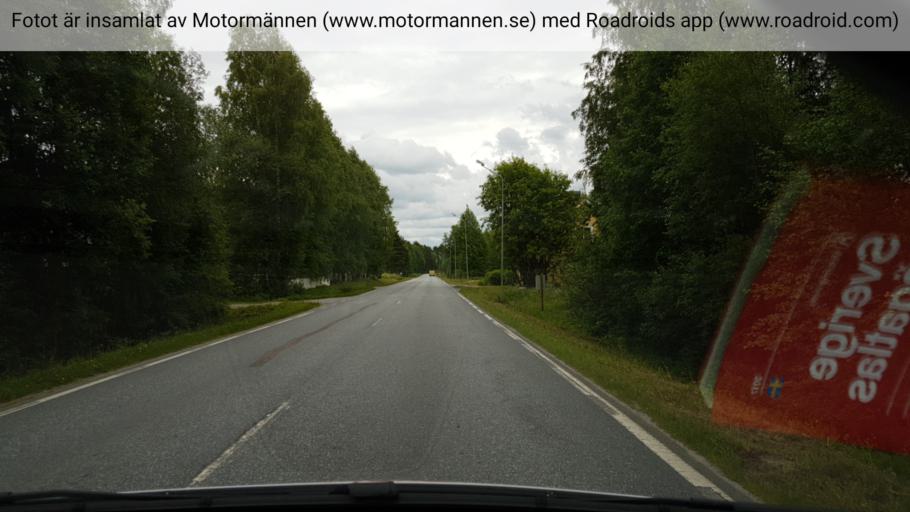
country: SE
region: Vaesternorrland
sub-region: Solleftea Kommun
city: As
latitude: 63.6967
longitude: 16.8498
